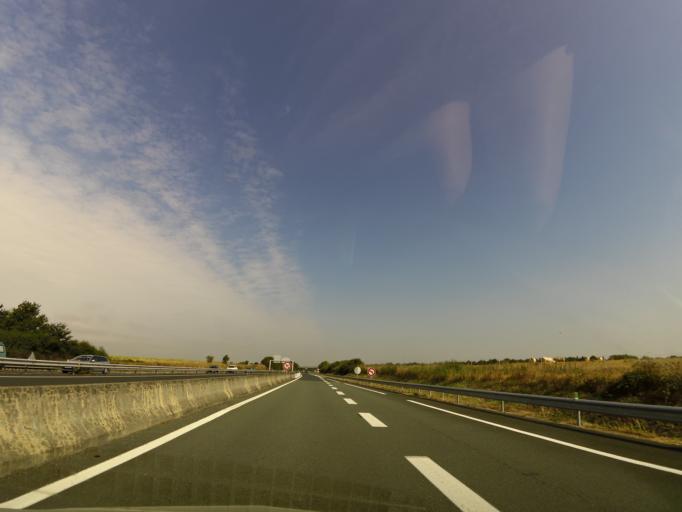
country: FR
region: Pays de la Loire
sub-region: Departement de la Vendee
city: Les Essarts
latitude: 46.8129
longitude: -1.2116
